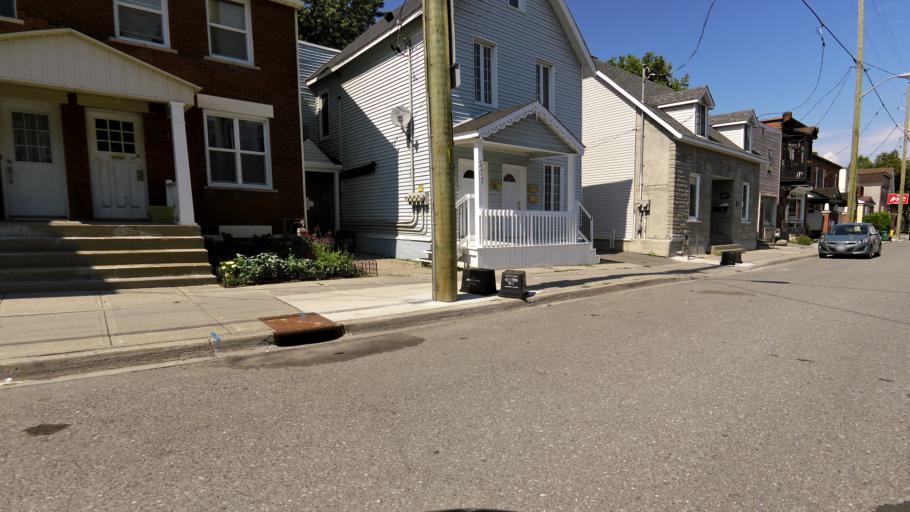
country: CA
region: Ontario
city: Ottawa
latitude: 45.4312
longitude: -75.6921
